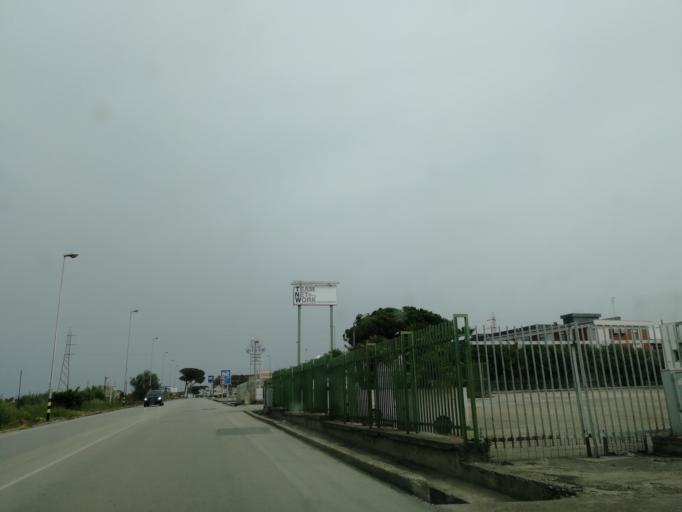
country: IT
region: Apulia
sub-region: Provincia di Barletta - Andria - Trani
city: Barletta
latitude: 41.3146
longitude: 16.3016
